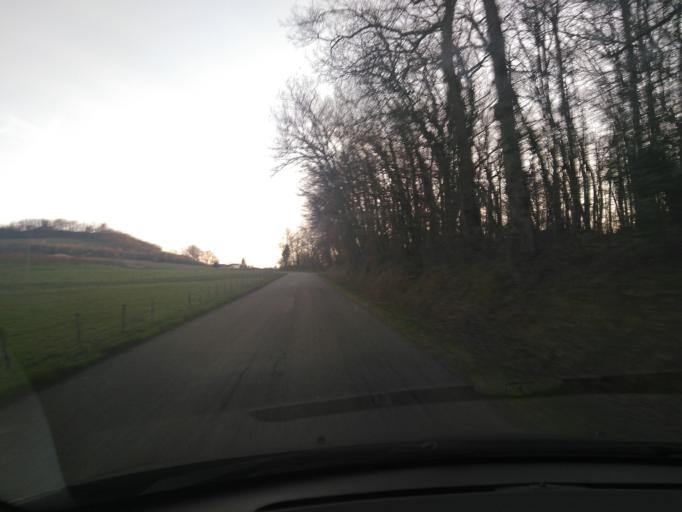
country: FR
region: Aquitaine
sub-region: Departement du Lot-et-Garonne
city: Saint-Hilaire
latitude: 44.5255
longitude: 0.6878
